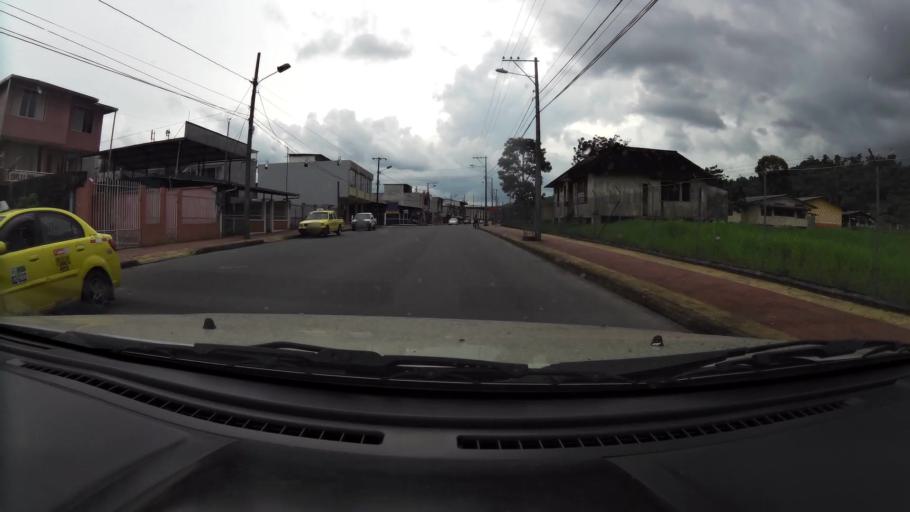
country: EC
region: Pastaza
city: Puyo
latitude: -1.4904
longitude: -78.0127
